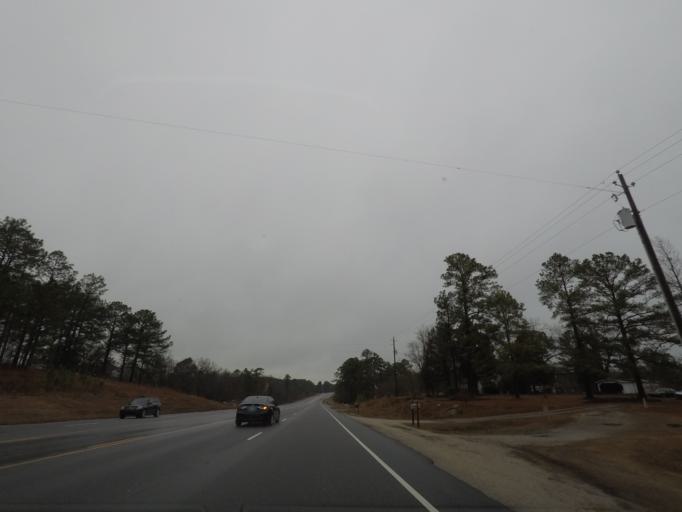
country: US
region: North Carolina
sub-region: Lee County
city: Broadway
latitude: 35.3463
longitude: -79.1067
